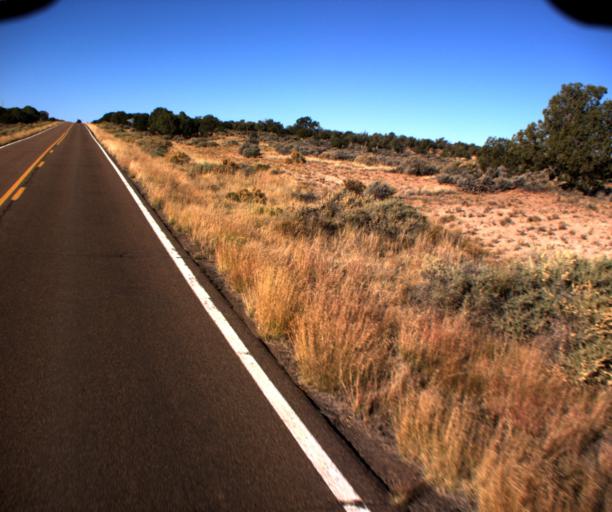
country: US
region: Arizona
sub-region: Apache County
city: Ganado
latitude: 35.7534
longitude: -109.9017
